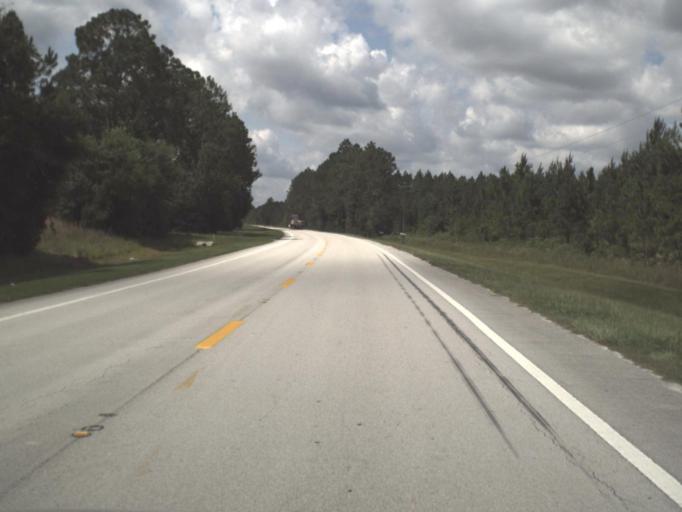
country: US
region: Florida
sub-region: Baker County
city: Macclenny
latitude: 30.2170
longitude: -82.1522
